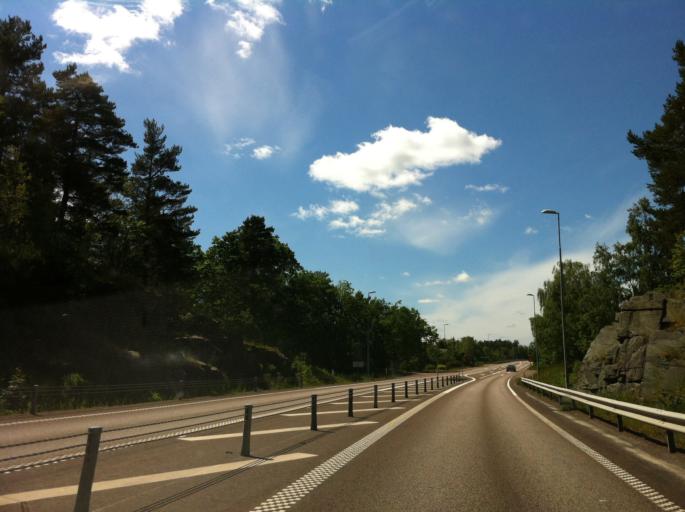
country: SE
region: Vaestra Goetaland
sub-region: Melleruds Kommun
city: Mellerud
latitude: 58.7831
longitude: 12.5116
